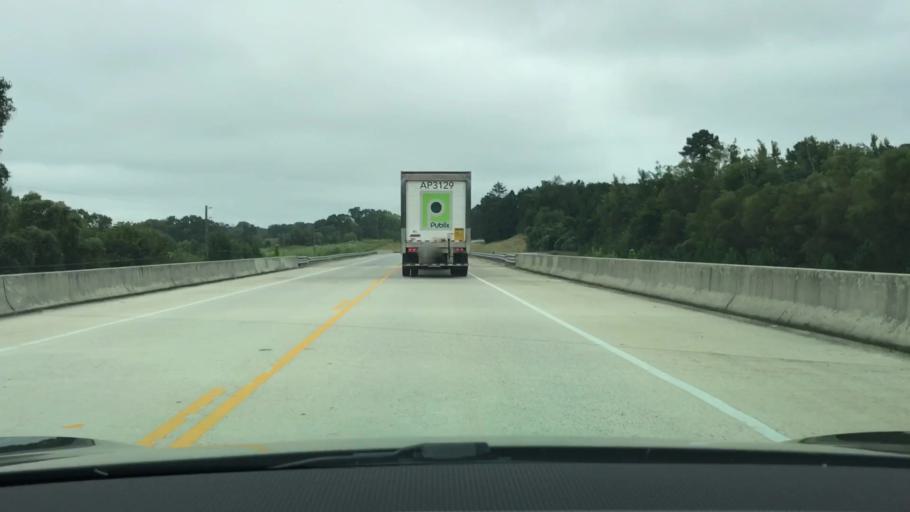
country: US
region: Georgia
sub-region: Oconee County
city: Watkinsville
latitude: 33.7350
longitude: -83.3033
